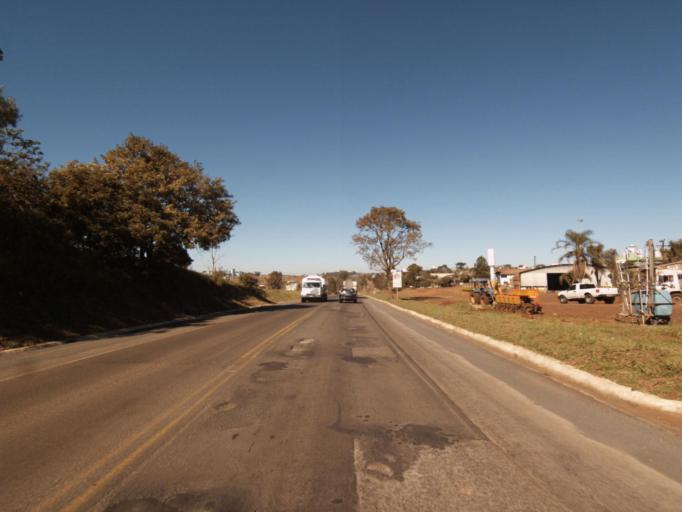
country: BR
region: Santa Catarina
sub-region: Chapeco
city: Chapeco
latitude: -26.8403
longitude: -52.9836
